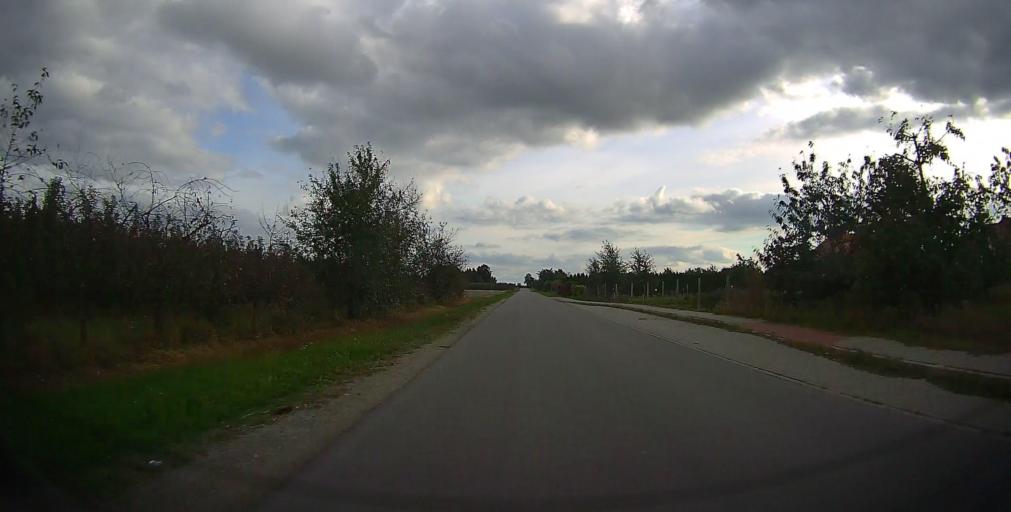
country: PL
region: Masovian Voivodeship
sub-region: Powiat bialobrzeski
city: Promna
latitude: 51.7216
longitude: 20.9586
